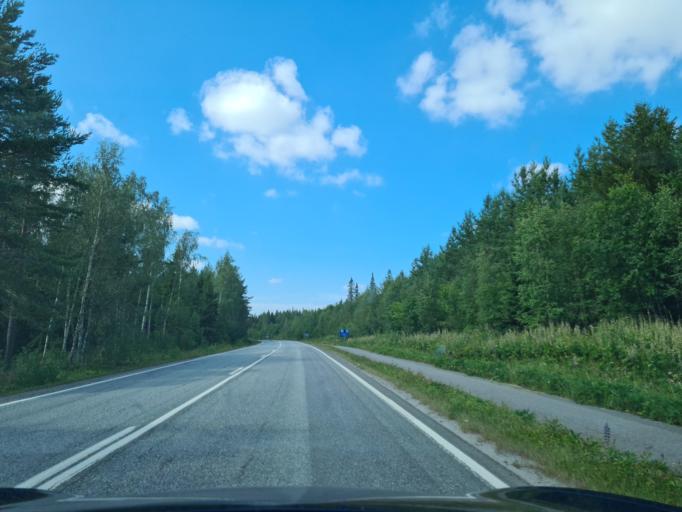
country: FI
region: Ostrobothnia
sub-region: Vaasa
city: Replot
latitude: 63.2026
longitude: 21.5282
